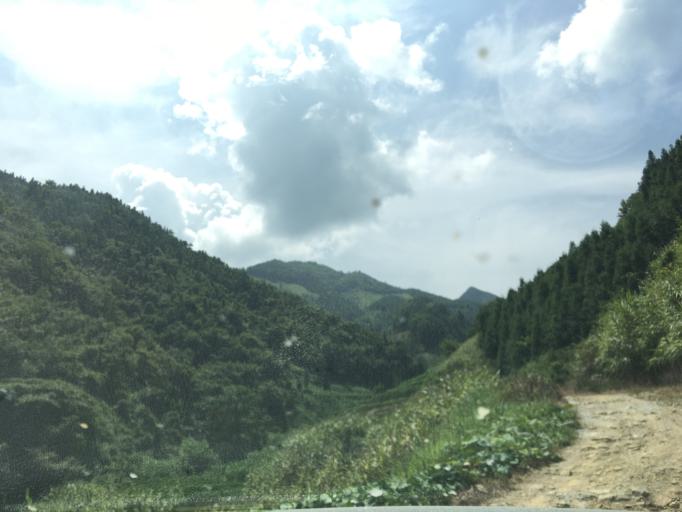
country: CN
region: Guangxi Zhuangzu Zizhiqu
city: Xinzhou
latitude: 24.9533
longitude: 105.7898
